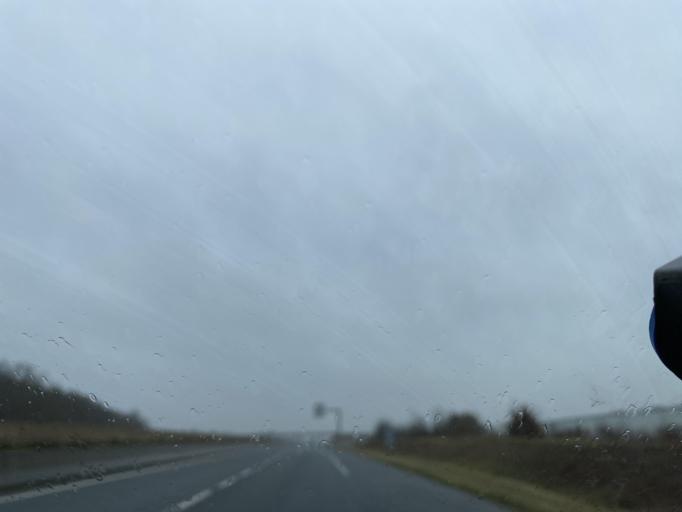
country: FR
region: Centre
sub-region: Departement d'Eure-et-Loir
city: Villemeux-sur-Eure
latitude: 48.6101
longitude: 1.4196
